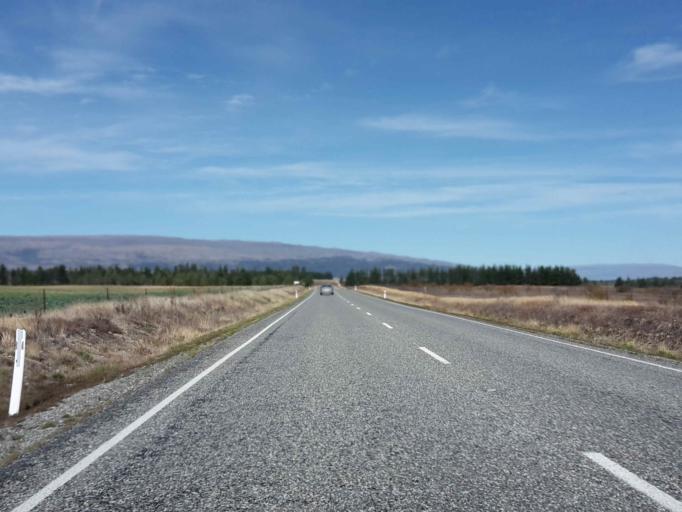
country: NZ
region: Otago
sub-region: Queenstown-Lakes District
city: Wanaka
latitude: -44.8013
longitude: 169.3564
